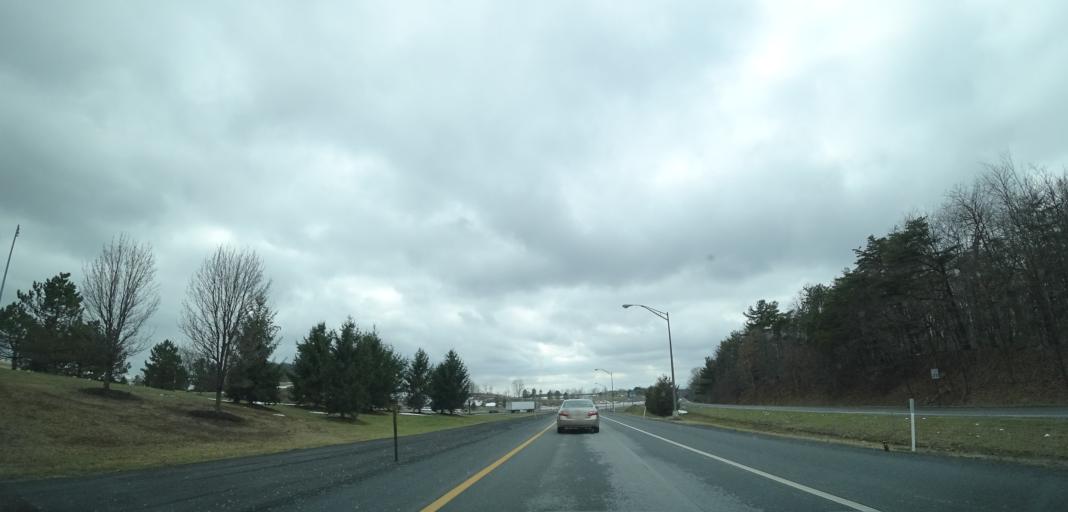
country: US
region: Pennsylvania
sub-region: Bedford County
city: Earlston
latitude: 39.9882
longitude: -78.2566
